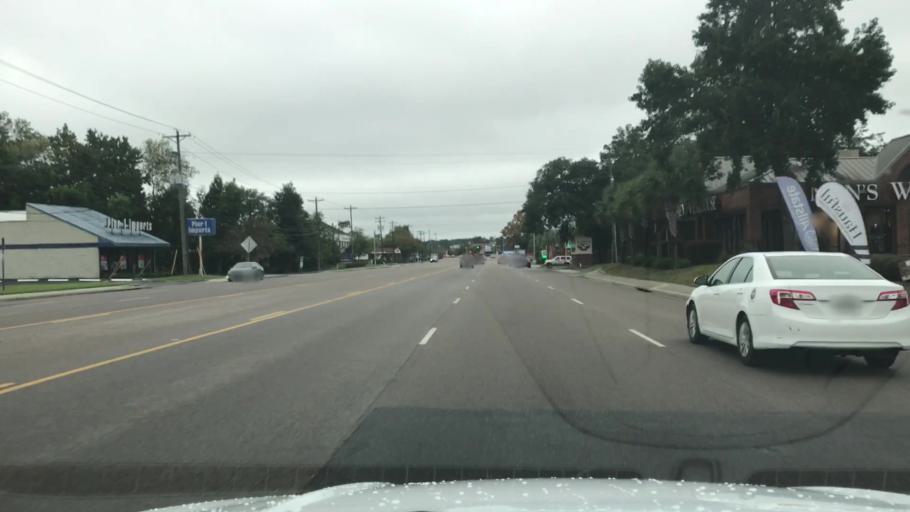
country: US
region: South Carolina
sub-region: Charleston County
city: North Charleston
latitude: 32.7989
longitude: -80.0222
